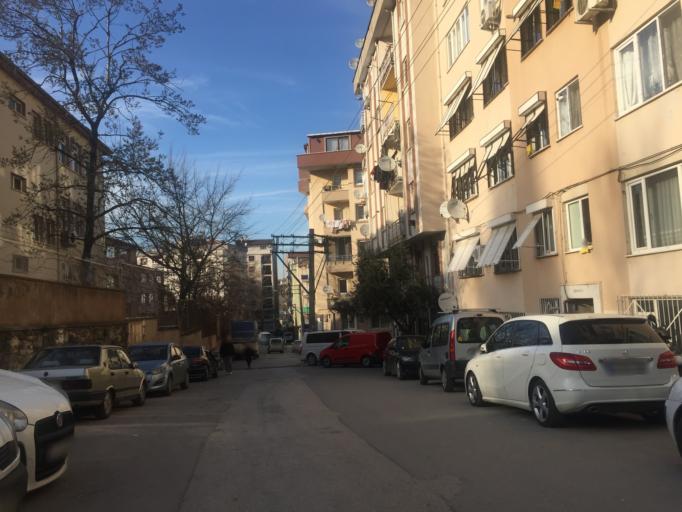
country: TR
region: Bursa
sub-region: Osmangazi
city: Bursa
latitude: 40.1887
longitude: 29.0832
